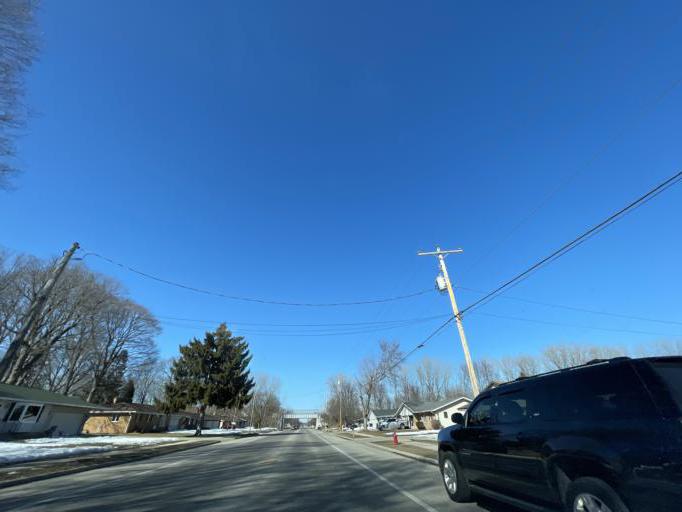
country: US
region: Wisconsin
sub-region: Brown County
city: Howard
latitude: 44.5777
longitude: -88.0847
